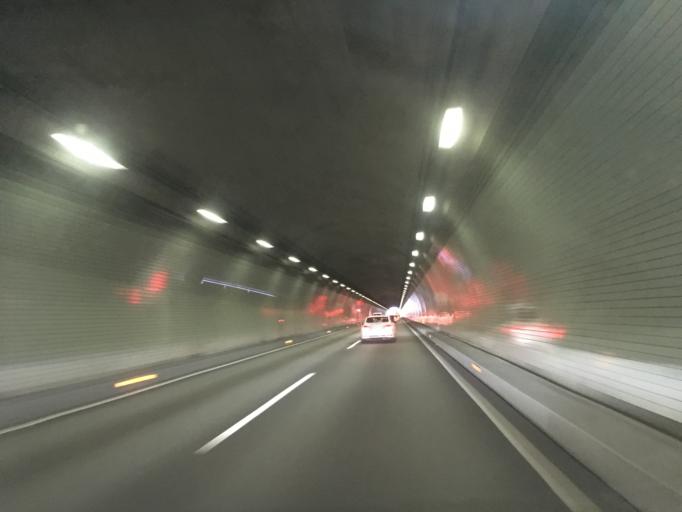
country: JP
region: Tokyo
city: Fussa
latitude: 35.7662
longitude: 139.2882
